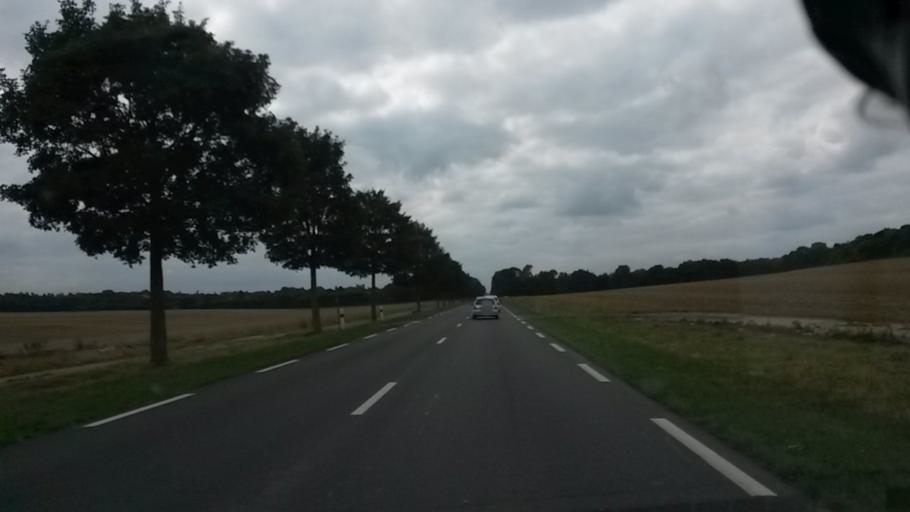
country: FR
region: Picardie
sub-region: Departement de la Somme
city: Camon
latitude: 49.9318
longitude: 2.4064
